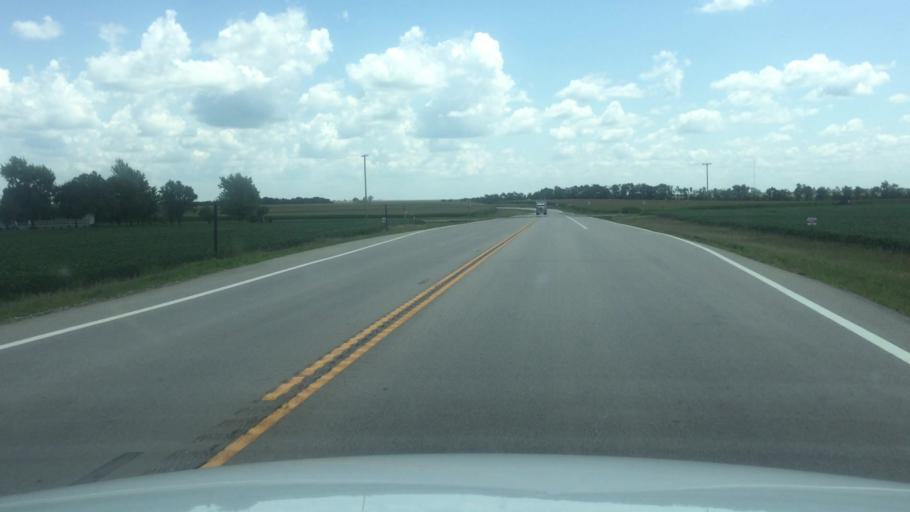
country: US
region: Kansas
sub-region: Brown County
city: Horton
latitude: 39.6648
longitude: -95.4167
